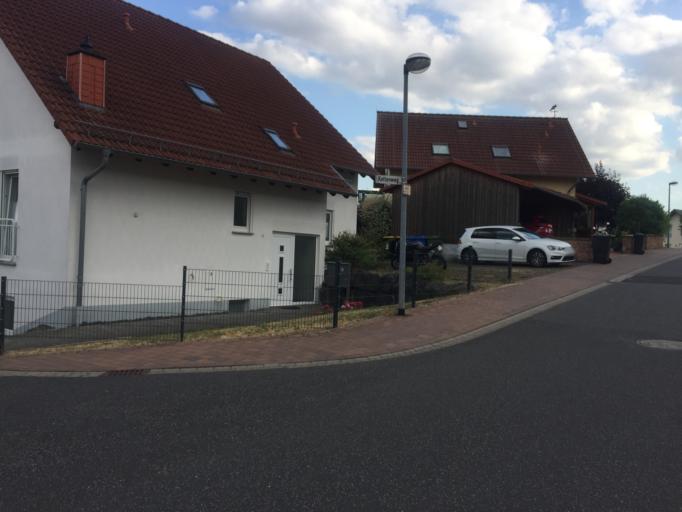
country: DE
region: Hesse
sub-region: Regierungsbezirk Giessen
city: Heuchelheim
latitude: 50.6411
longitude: 8.5929
